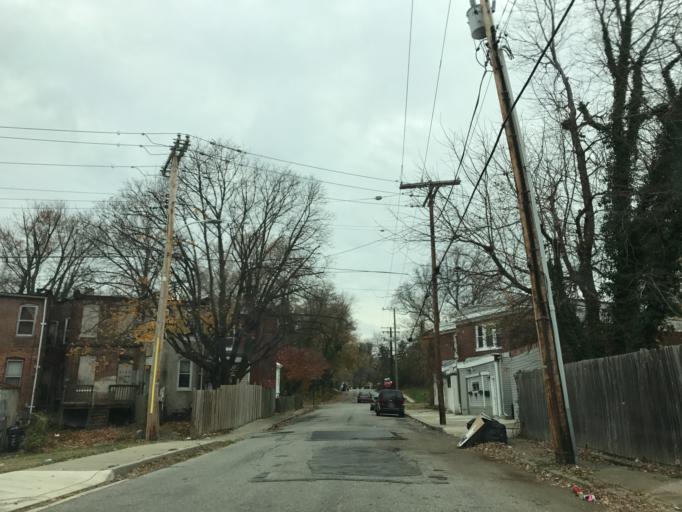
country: US
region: Maryland
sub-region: Baltimore County
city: Woodlawn
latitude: 39.3128
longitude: -76.6801
